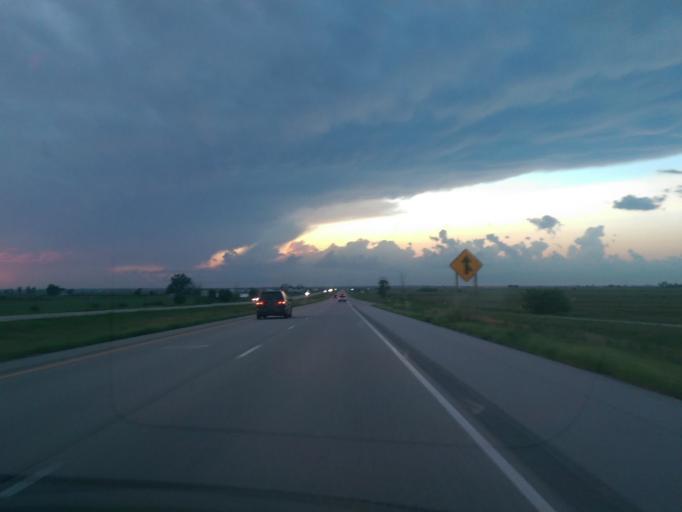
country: US
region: Nebraska
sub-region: Otoe County
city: Nebraska City
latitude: 40.6908
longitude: -95.7840
